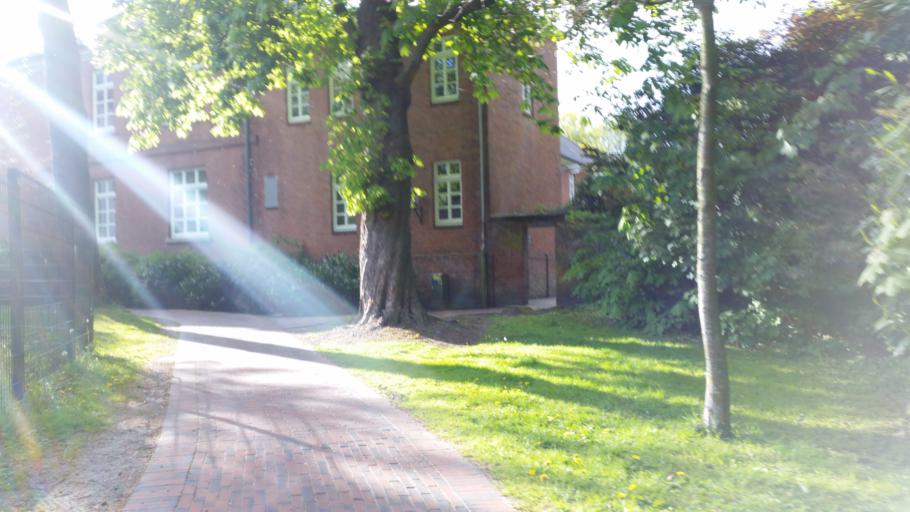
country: DE
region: Lower Saxony
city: Aurich
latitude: 53.4682
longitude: 7.4790
